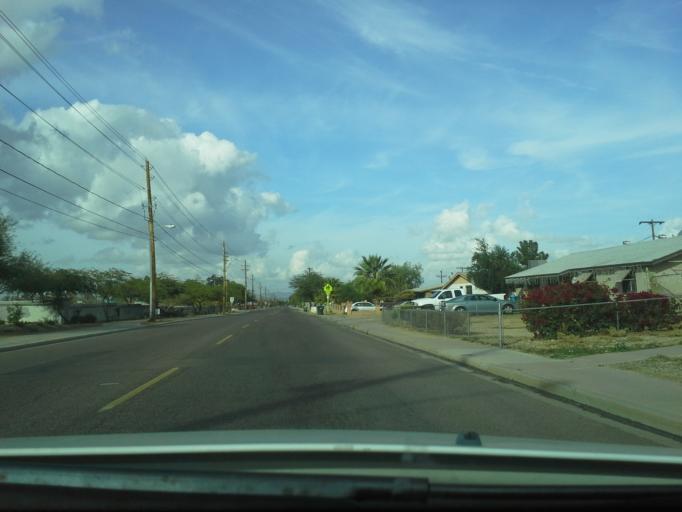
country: US
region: Arizona
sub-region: Maricopa County
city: Phoenix
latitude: 33.3687
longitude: -112.0833
